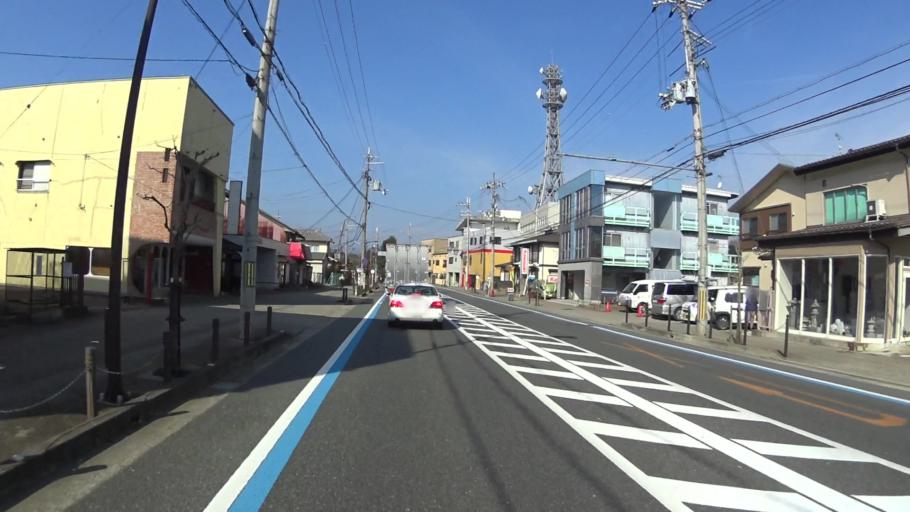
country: JP
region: Kyoto
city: Fukuchiyama
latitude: 35.2966
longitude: 135.1323
